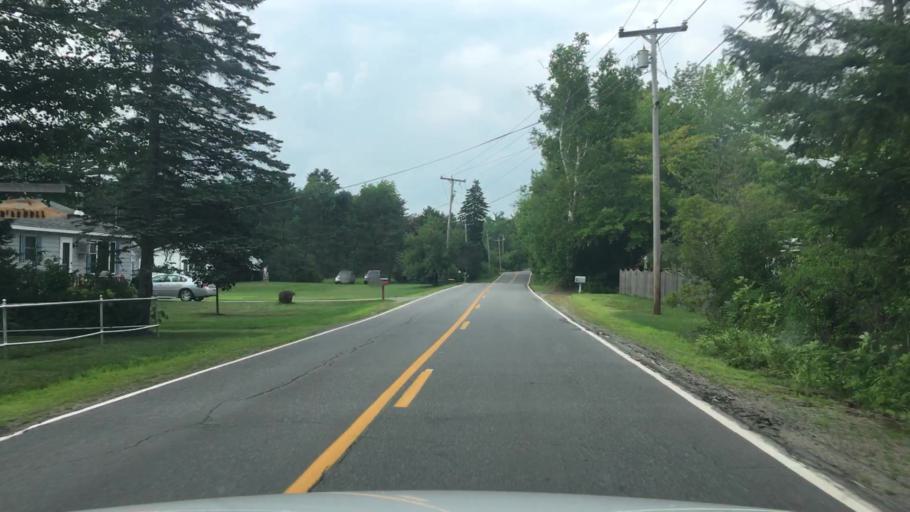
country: US
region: Maine
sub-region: Knox County
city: Washington
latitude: 44.2966
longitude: -69.3622
